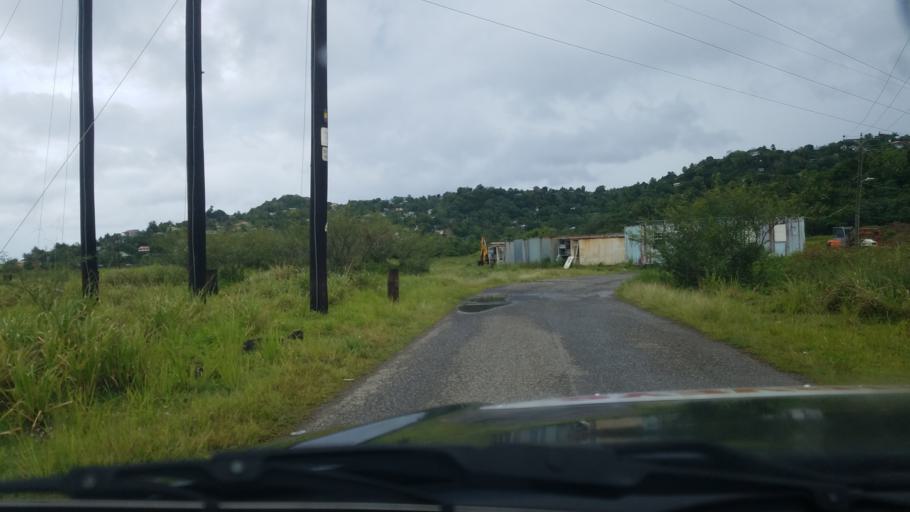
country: LC
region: Castries Quarter
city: Castries
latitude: 13.9867
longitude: -60.9996
